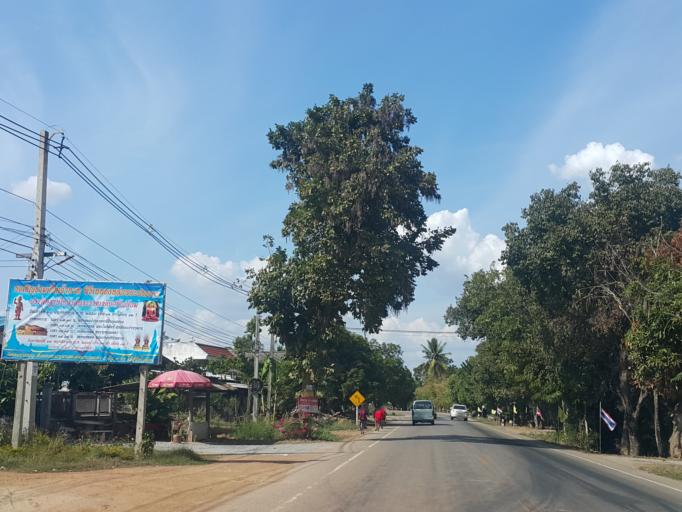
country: TH
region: Sukhothai
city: Sawankhalok
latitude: 17.2910
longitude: 99.8320
